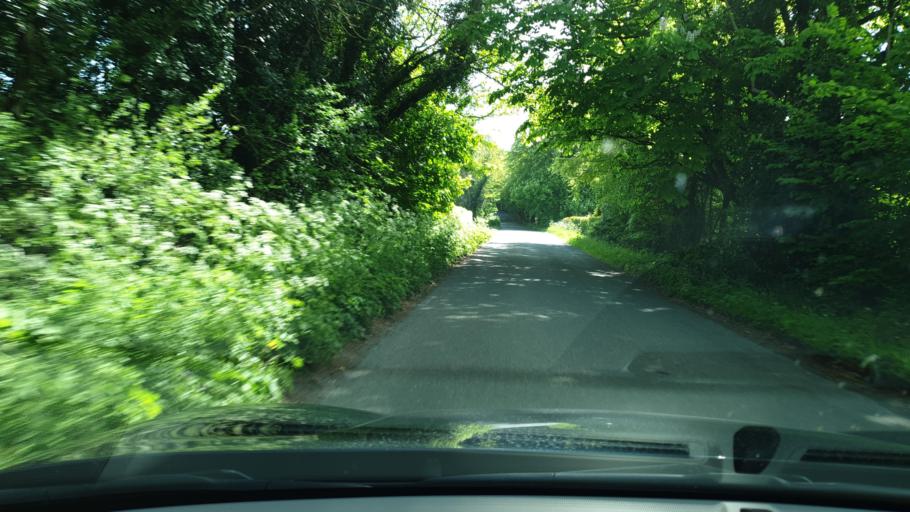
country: IE
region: Leinster
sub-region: An Mhi
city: Dunshaughlin
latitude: 53.4781
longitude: -6.5382
